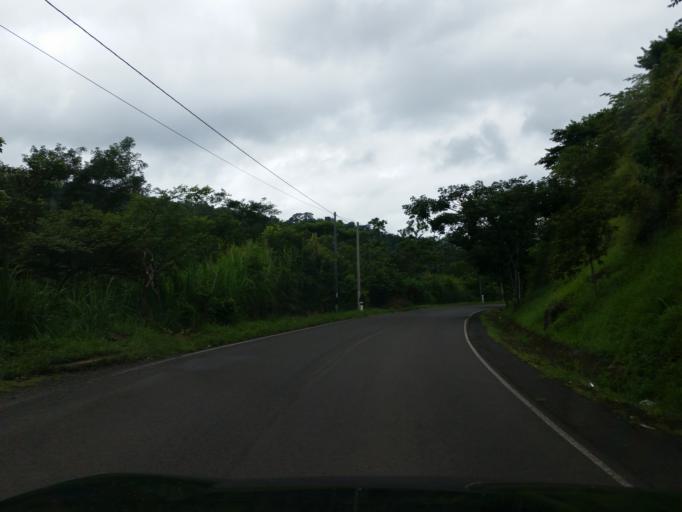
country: NI
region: Matagalpa
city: San Ramon
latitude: 12.9952
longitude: -85.8200
